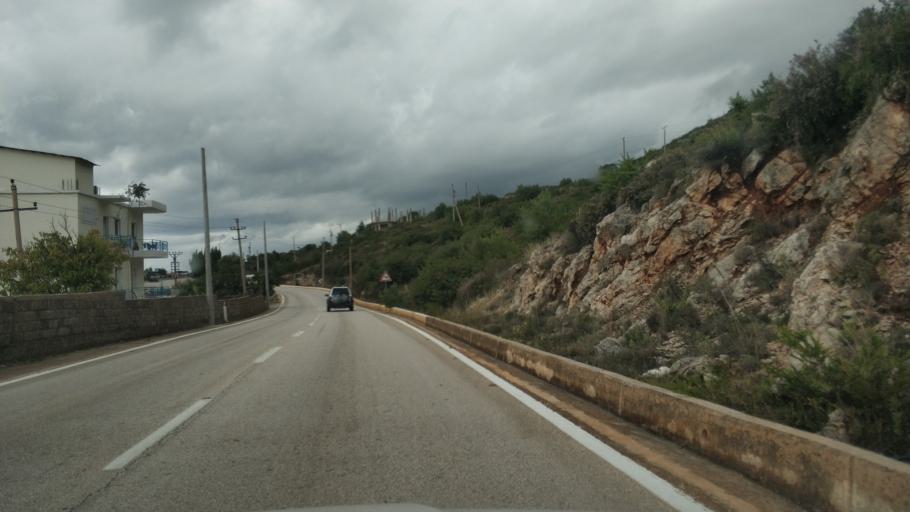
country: AL
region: Vlore
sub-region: Rrethi i Vlores
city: Vranisht
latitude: 40.1449
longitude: 19.6465
